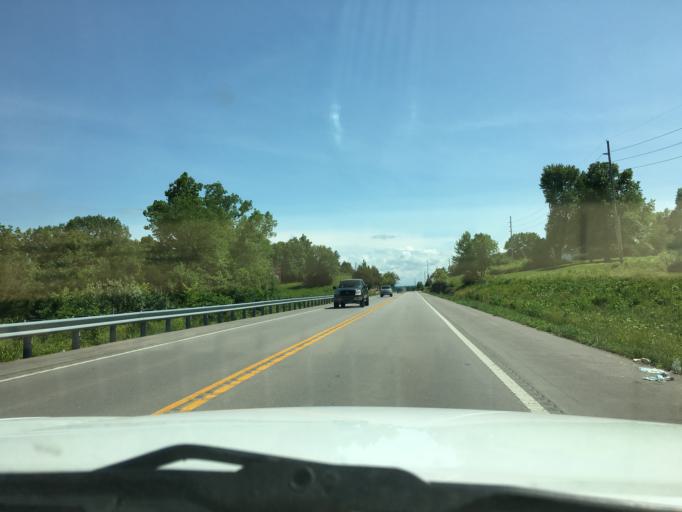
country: US
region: Missouri
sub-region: Franklin County
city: Union
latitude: 38.4757
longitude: -91.0056
